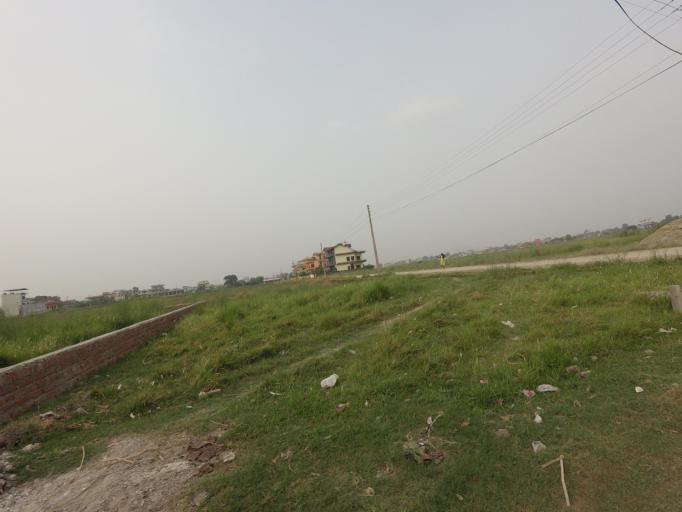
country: NP
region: Western Region
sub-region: Lumbini Zone
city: Bhairahawa
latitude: 27.5279
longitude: 83.4510
